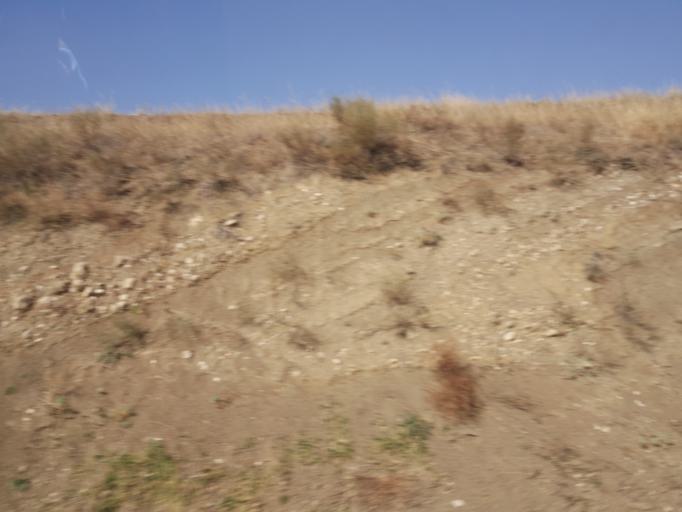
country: TR
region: Corum
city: Bogazkale
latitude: 40.1713
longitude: 34.6685
